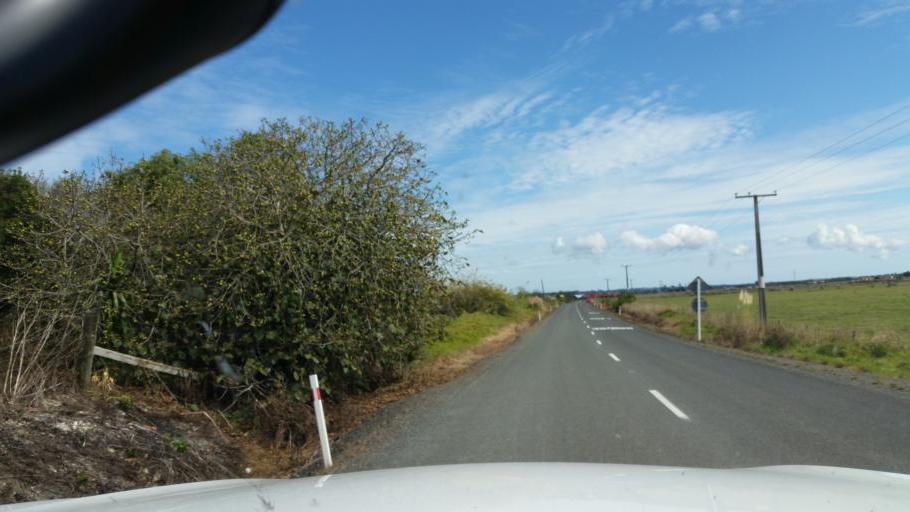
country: NZ
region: Northland
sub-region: Kaipara District
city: Dargaville
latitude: -36.1513
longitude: 174.0702
